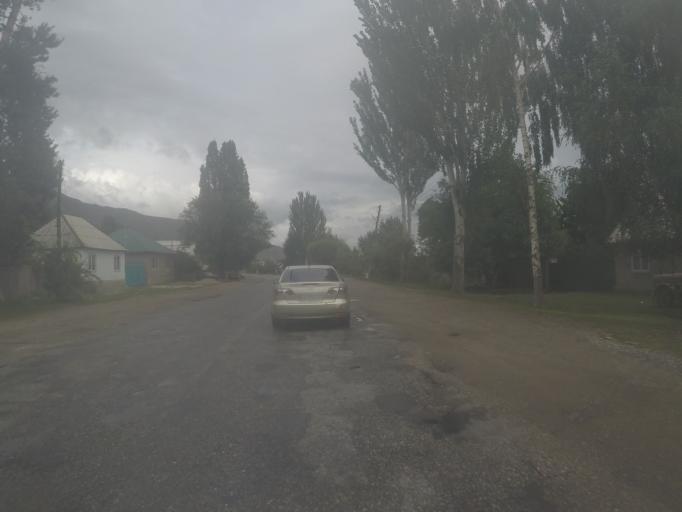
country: KG
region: Ysyk-Koel
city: Tyup
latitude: 42.7389
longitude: 78.0070
